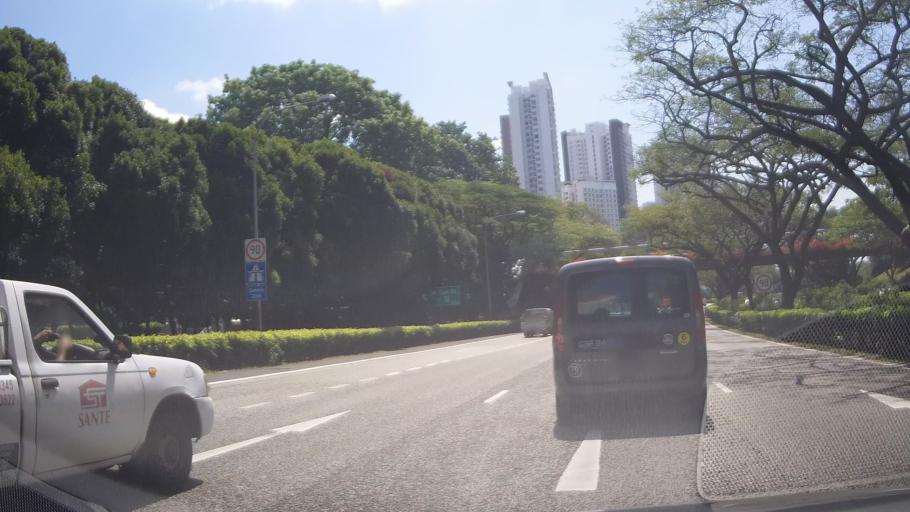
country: MY
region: Johor
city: Johor Bahru
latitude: 1.3450
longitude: 103.7413
